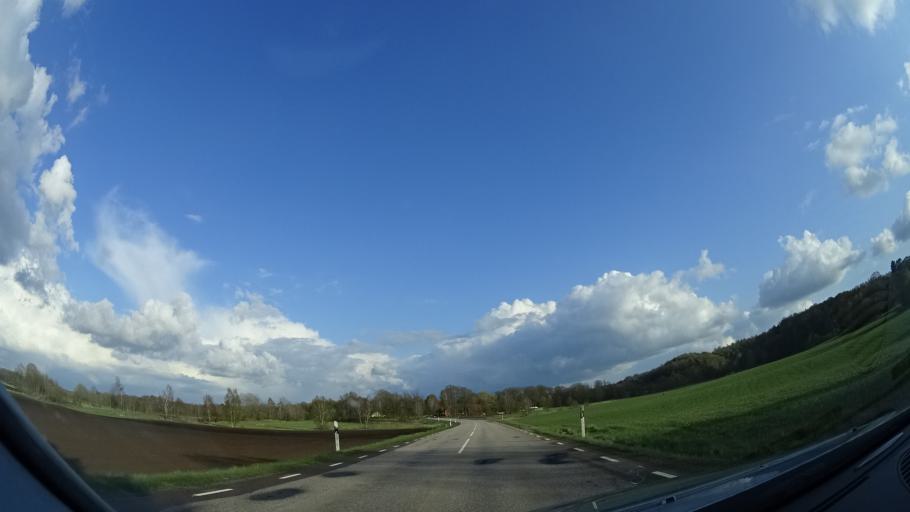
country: SE
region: Skane
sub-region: Klippans Kommun
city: Ljungbyhed
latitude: 56.0252
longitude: 13.2685
